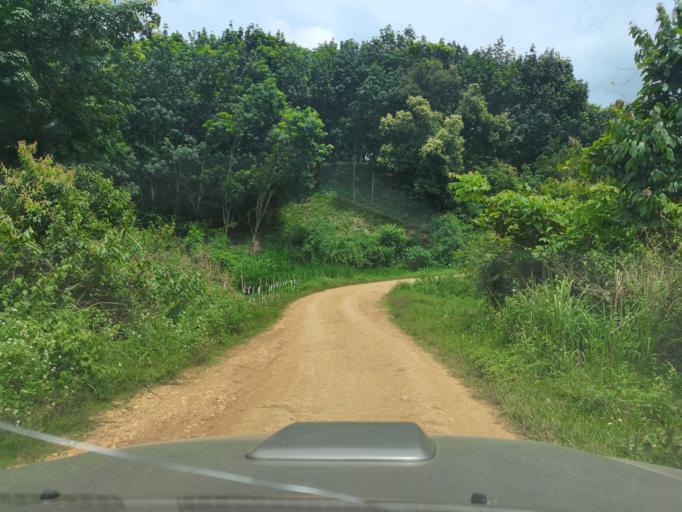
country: TH
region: Phayao
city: Phu Sang
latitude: 19.7208
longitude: 100.4854
